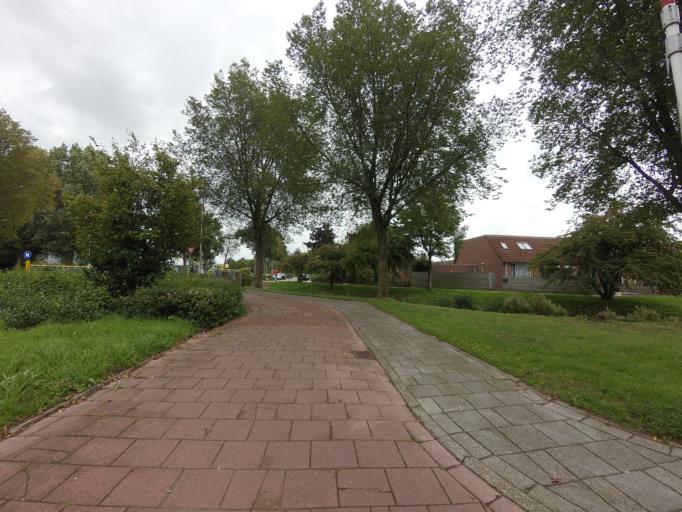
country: NL
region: North Holland
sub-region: Gemeente Purmerend
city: Purmerend
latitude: 52.5123
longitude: 4.9916
